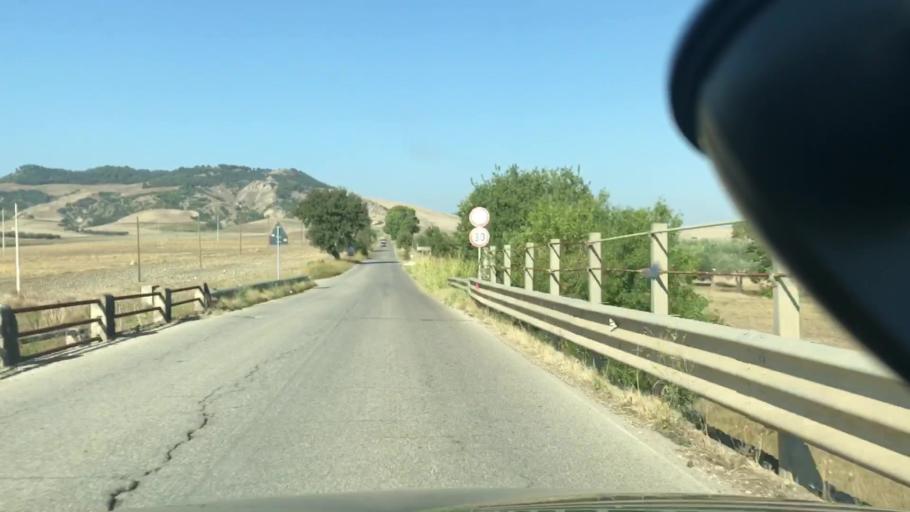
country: IT
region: Basilicate
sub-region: Provincia di Matera
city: La Martella
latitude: 40.6583
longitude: 16.5227
